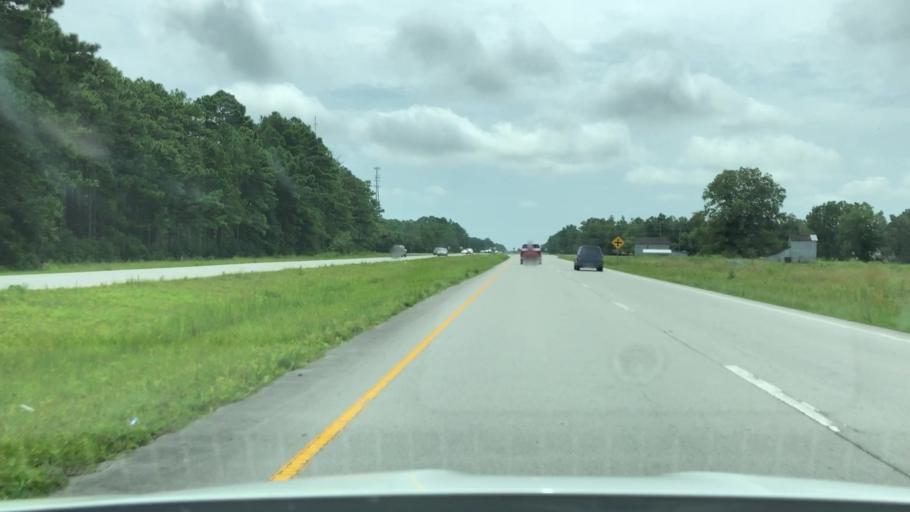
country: US
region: North Carolina
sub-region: Carteret County
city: Newport
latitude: 34.8079
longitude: -76.8793
